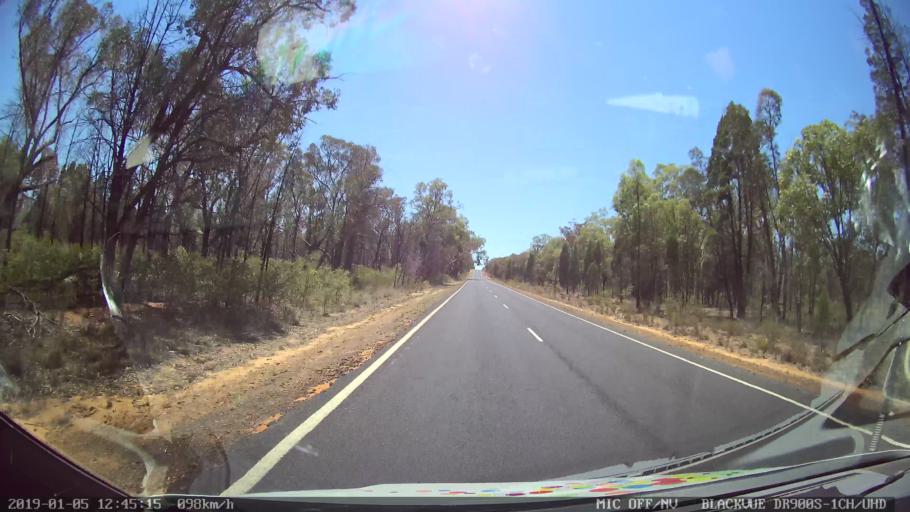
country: AU
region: New South Wales
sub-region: Warrumbungle Shire
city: Coonabarabran
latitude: -31.1297
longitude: 149.5476
